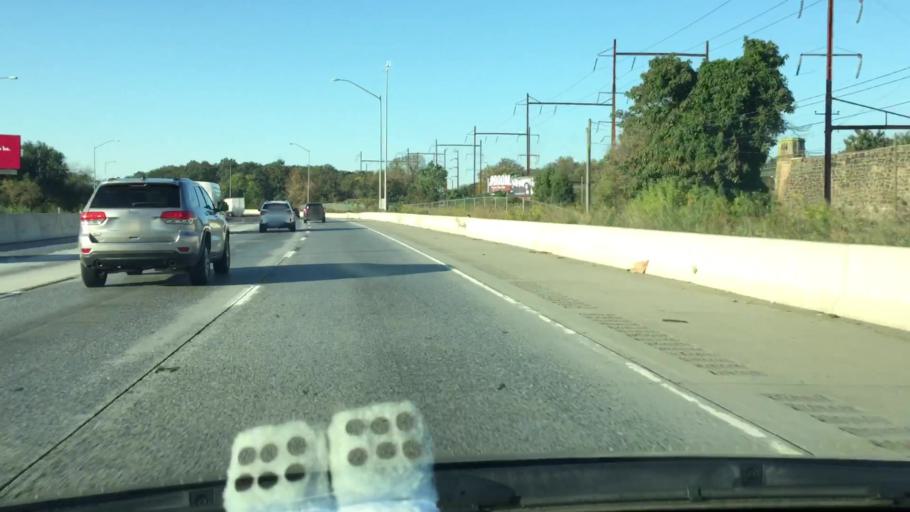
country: US
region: New Jersey
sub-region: Burlington County
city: Riverton
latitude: 40.0350
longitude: -75.0164
